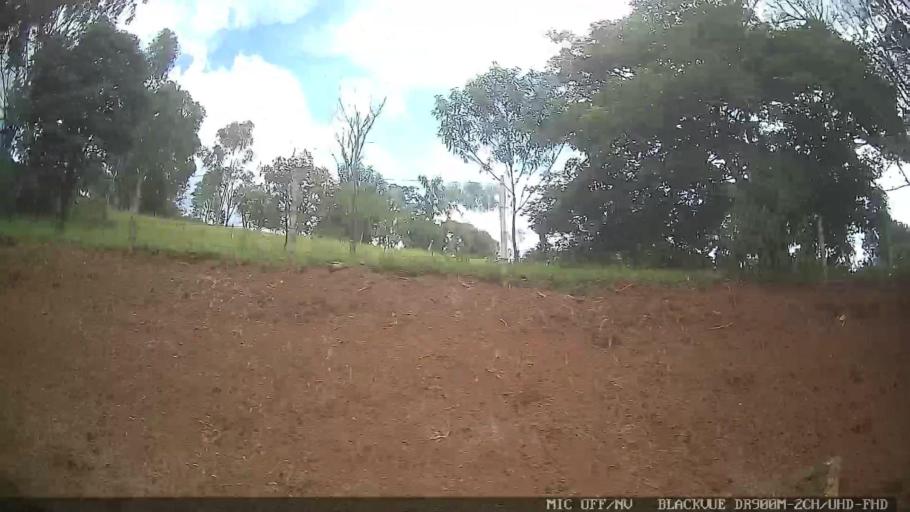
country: BR
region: Minas Gerais
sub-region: Extrema
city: Extrema
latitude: -22.8475
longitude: -46.2598
